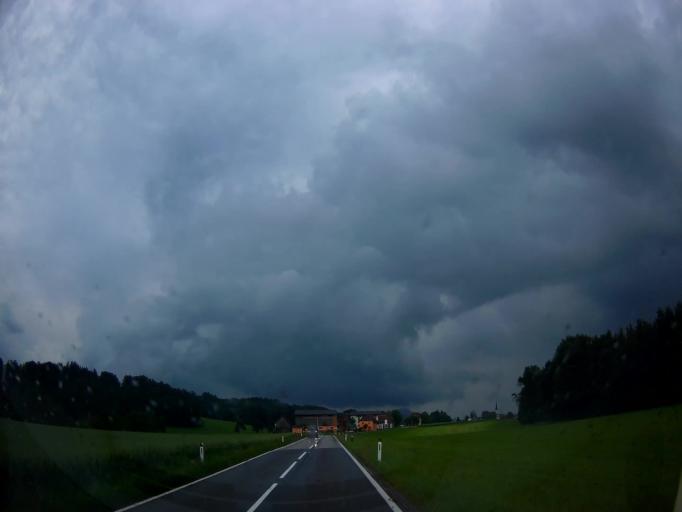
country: AT
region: Salzburg
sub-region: Politischer Bezirk Salzburg-Umgebung
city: Mattsee
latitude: 48.0231
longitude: 13.1328
